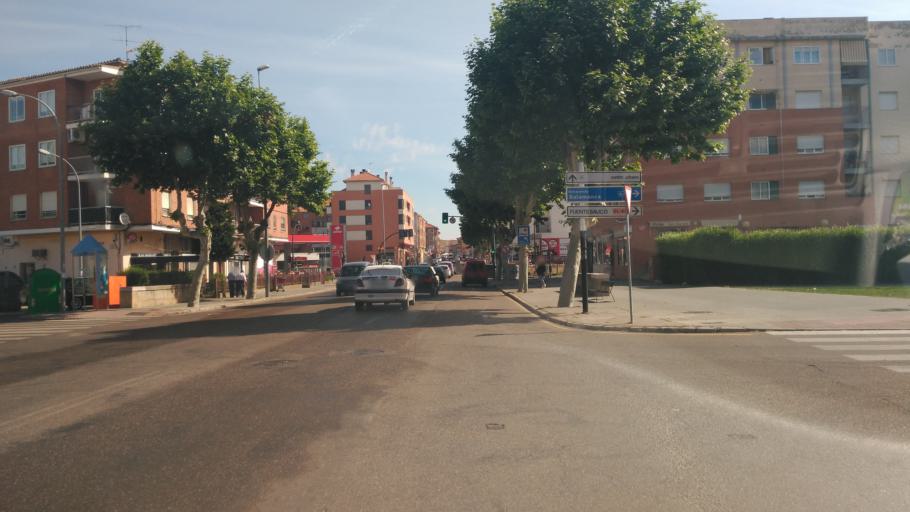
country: ES
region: Castille and Leon
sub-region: Provincia de Zamora
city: Zamora
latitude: 41.4940
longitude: -5.7418
